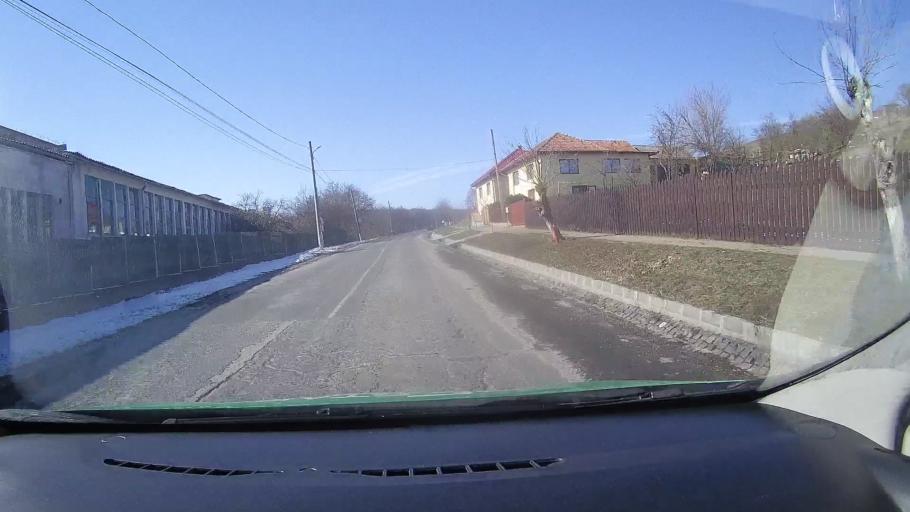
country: RO
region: Brasov
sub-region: Oras Rupea
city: Rupea
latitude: 46.0333
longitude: 25.2100
